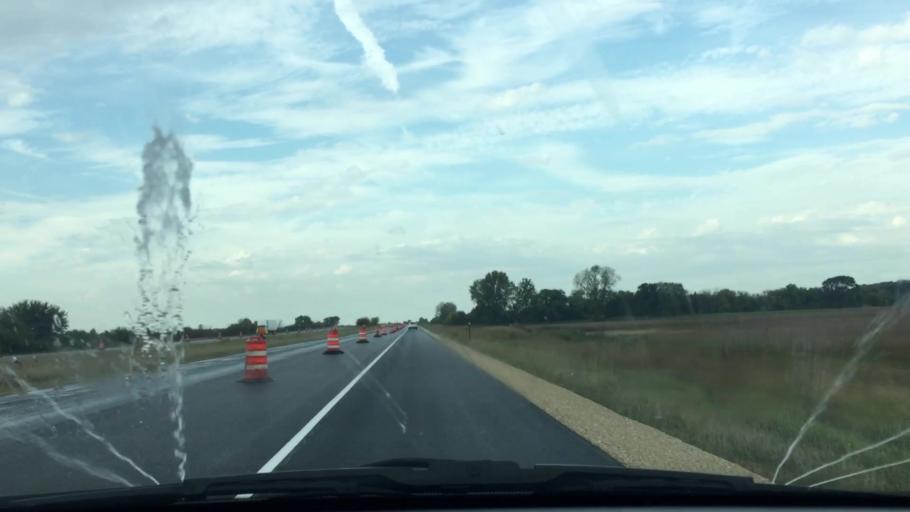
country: US
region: Illinois
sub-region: Whiteside County
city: Erie
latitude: 41.7099
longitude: -90.0201
